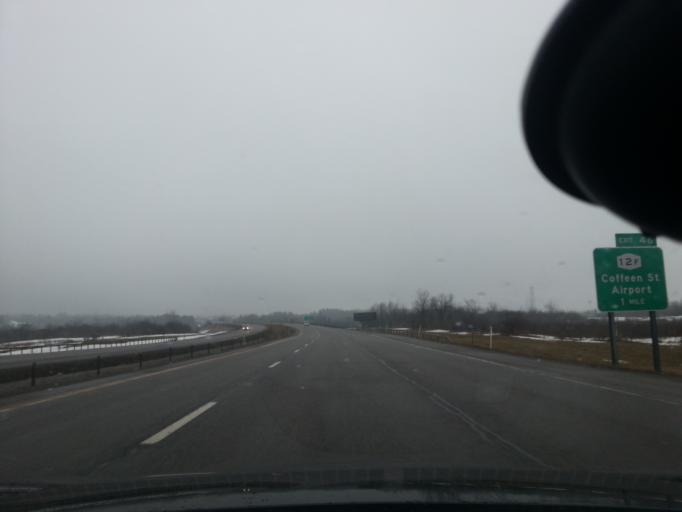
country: US
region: New York
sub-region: Jefferson County
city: Watertown
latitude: 44.0000
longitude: -75.9240
